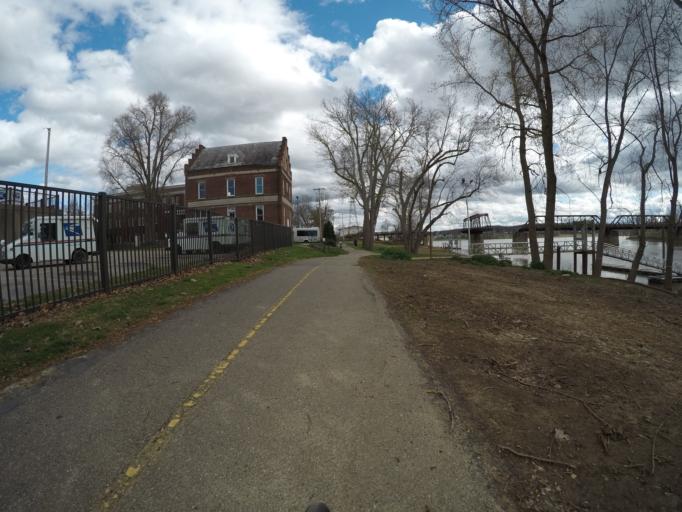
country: US
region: Ohio
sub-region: Washington County
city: Marietta
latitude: 39.4135
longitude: -81.4562
